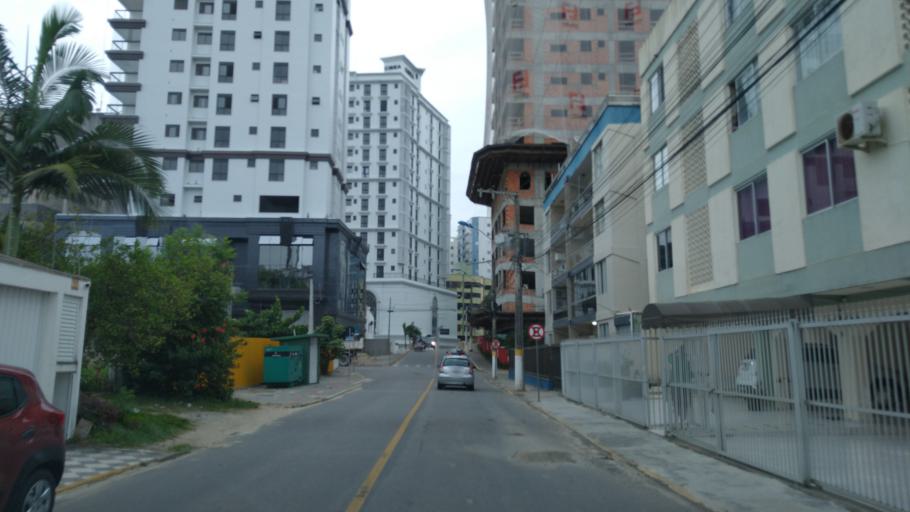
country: BR
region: Santa Catarina
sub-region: Itapema
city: Itapema
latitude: -27.0936
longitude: -48.6123
